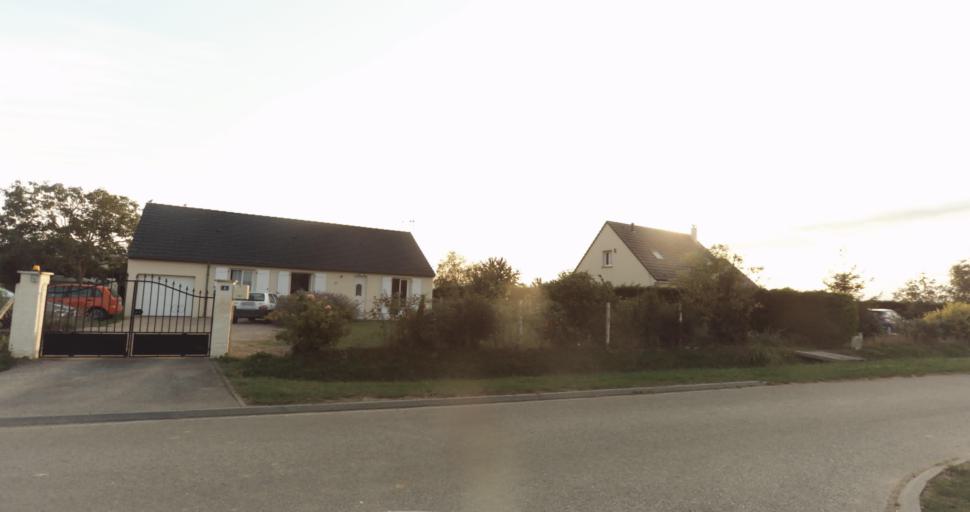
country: FR
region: Haute-Normandie
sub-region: Departement de l'Eure
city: La Madeleine-de-Nonancourt
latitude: 48.8535
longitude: 1.2145
